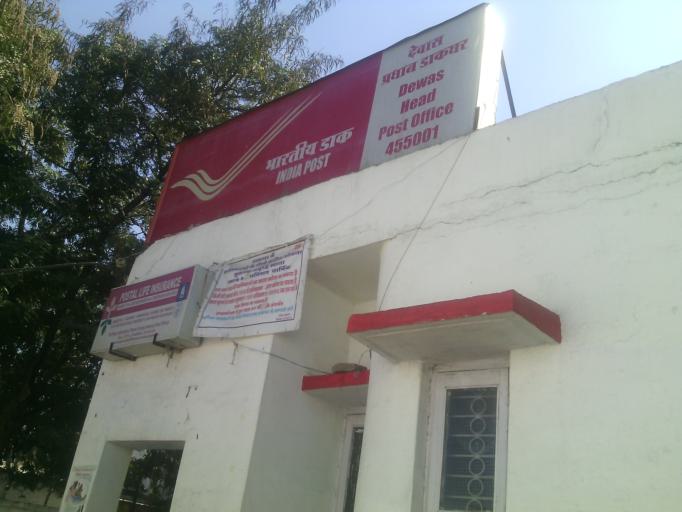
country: IN
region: Madhya Pradesh
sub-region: Dewas
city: Dewas
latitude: 22.9675
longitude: 76.0536
